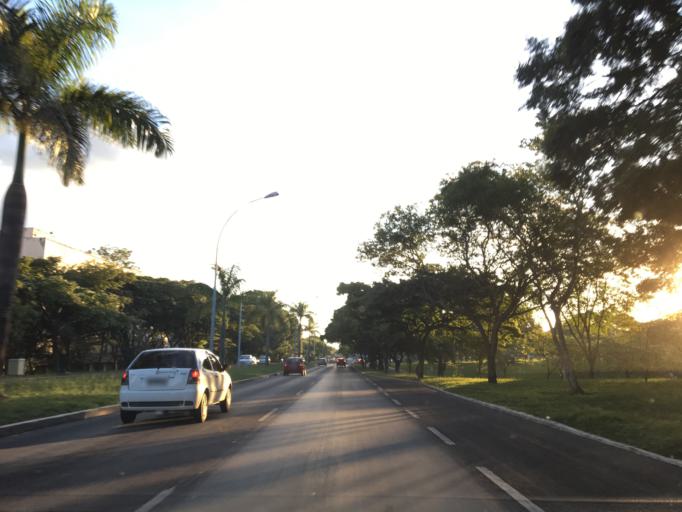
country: BR
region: Federal District
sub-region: Brasilia
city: Brasilia
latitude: -15.8220
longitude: -47.9067
